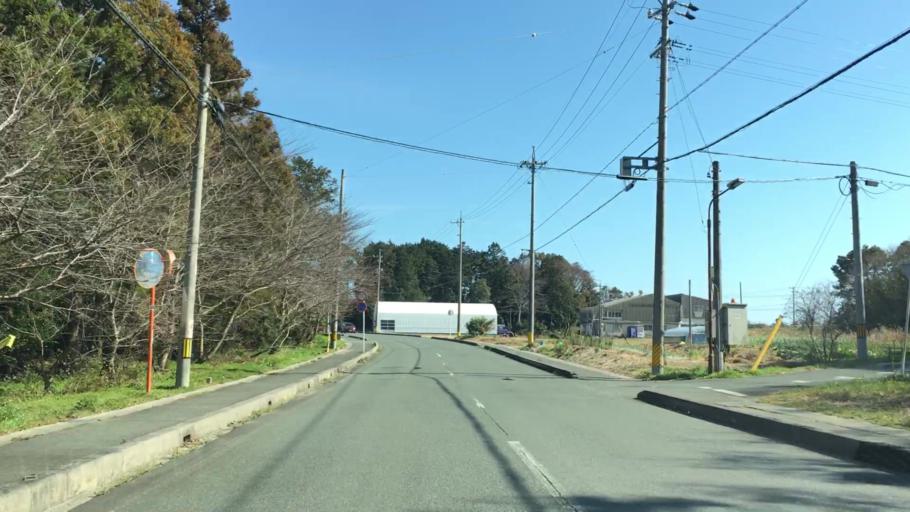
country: JP
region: Aichi
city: Tahara
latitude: 34.6599
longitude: 137.2801
